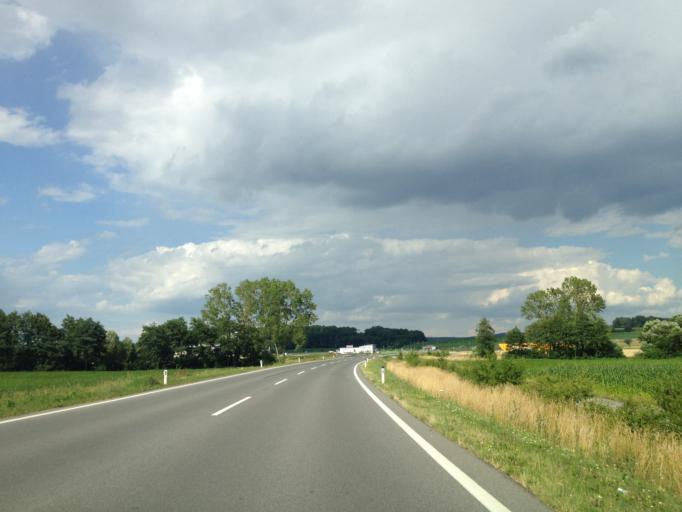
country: AT
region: Burgenland
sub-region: Politischer Bezirk Oberwart
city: Oberwart
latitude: 47.3014
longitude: 16.1853
